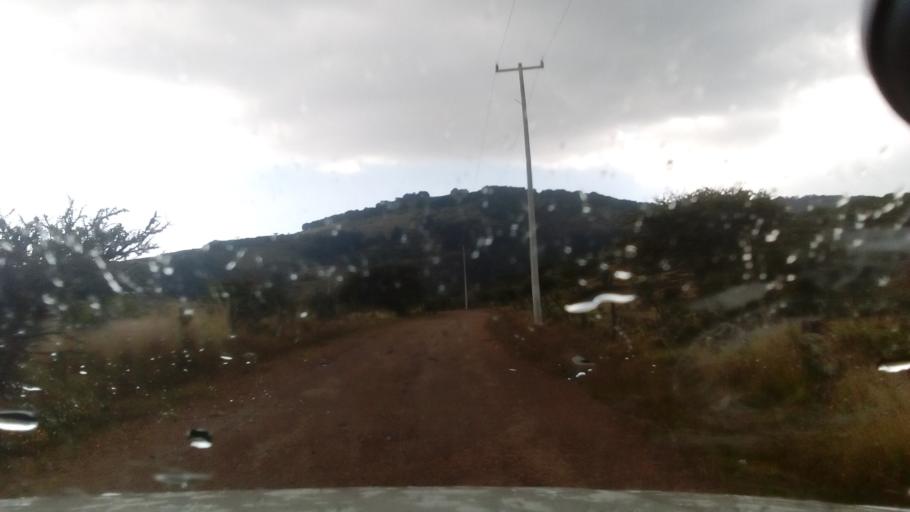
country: MX
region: Guanajuato
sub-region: Silao de la Victoria
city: San Francisco (Banos de Agua Caliente)
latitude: 21.1588
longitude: -101.4345
